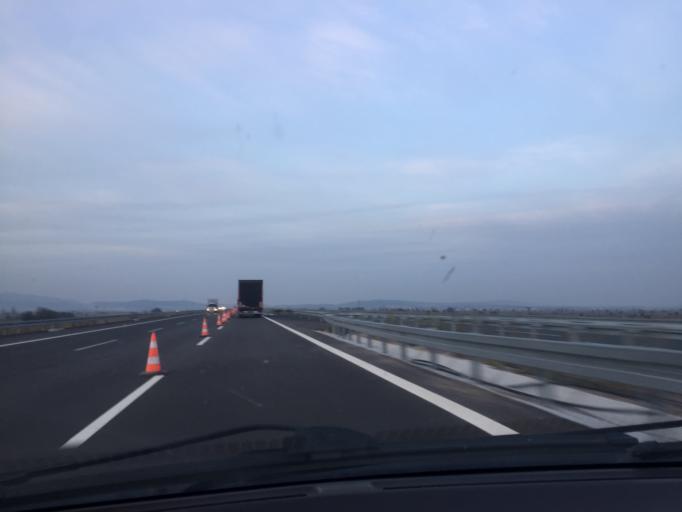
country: TR
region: Manisa
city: Halitpasa
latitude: 38.7298
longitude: 27.6551
